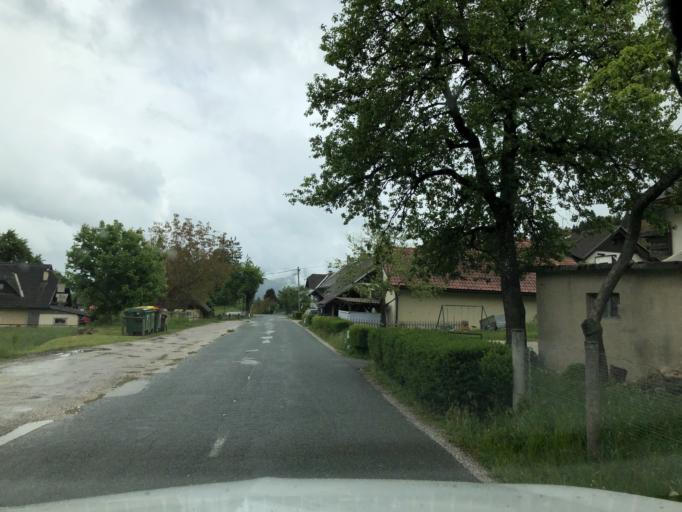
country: SI
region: Gorje
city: Zgornje Gorje
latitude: 46.3950
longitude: 14.0729
